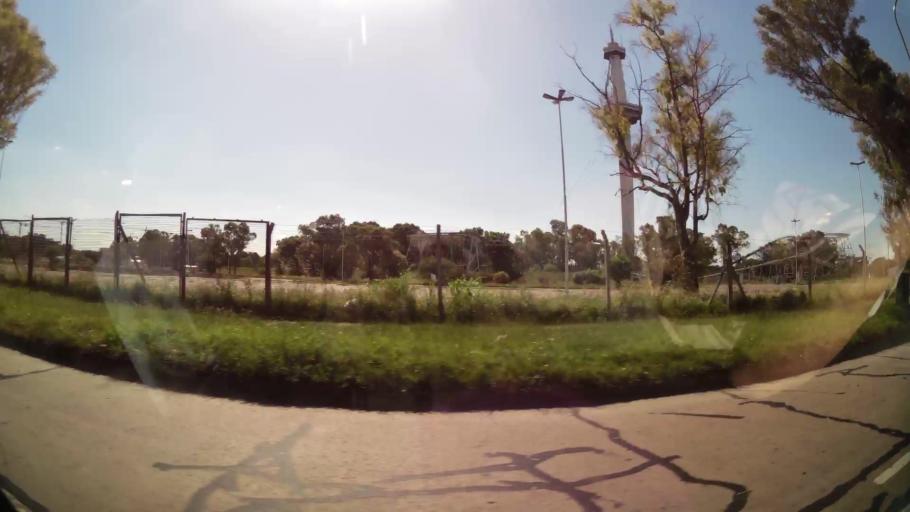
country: AR
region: Buenos Aires F.D.
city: Villa Lugano
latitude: -34.6753
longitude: -58.4477
